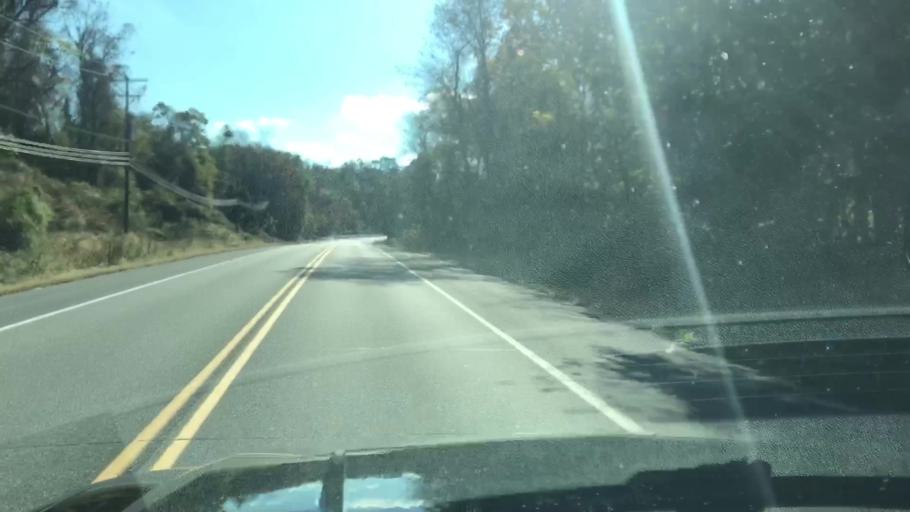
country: US
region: Pennsylvania
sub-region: Cumberland County
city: Lower Allen
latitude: 40.1672
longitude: -76.8877
